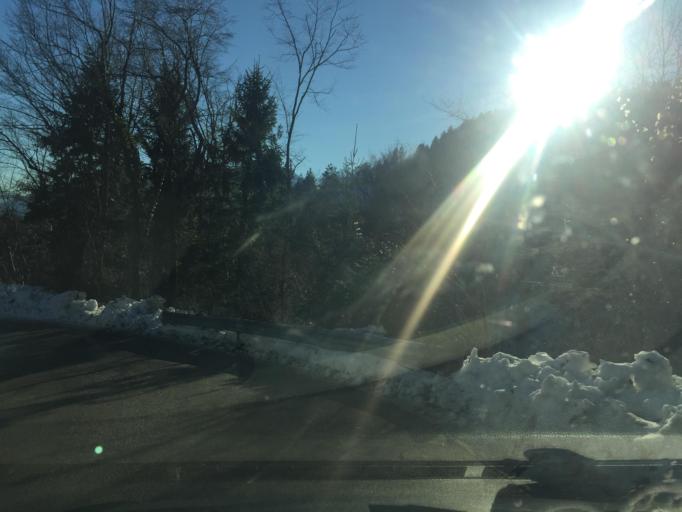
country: IT
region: Friuli Venezia Giulia
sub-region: Provincia di Udine
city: Tolmezzo
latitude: 46.4183
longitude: 13.0001
